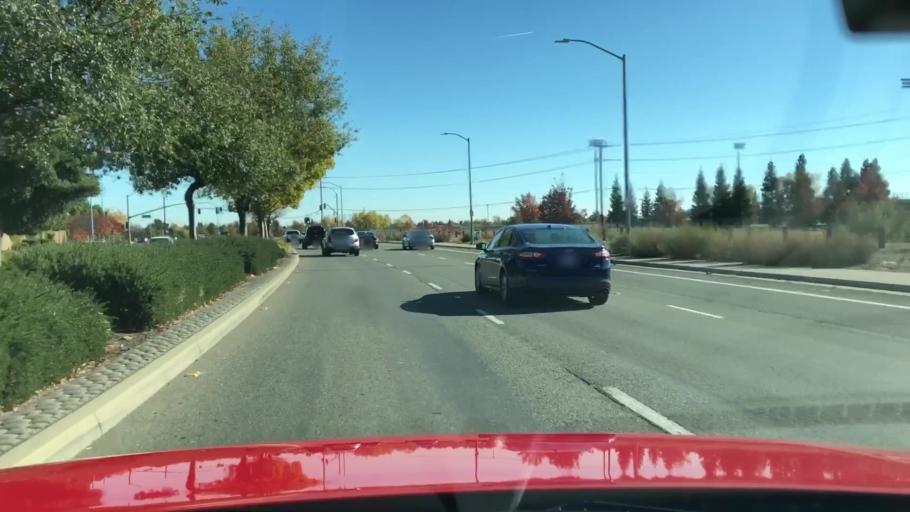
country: US
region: California
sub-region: Sacramento County
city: Laguna
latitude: 38.4538
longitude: -121.3977
